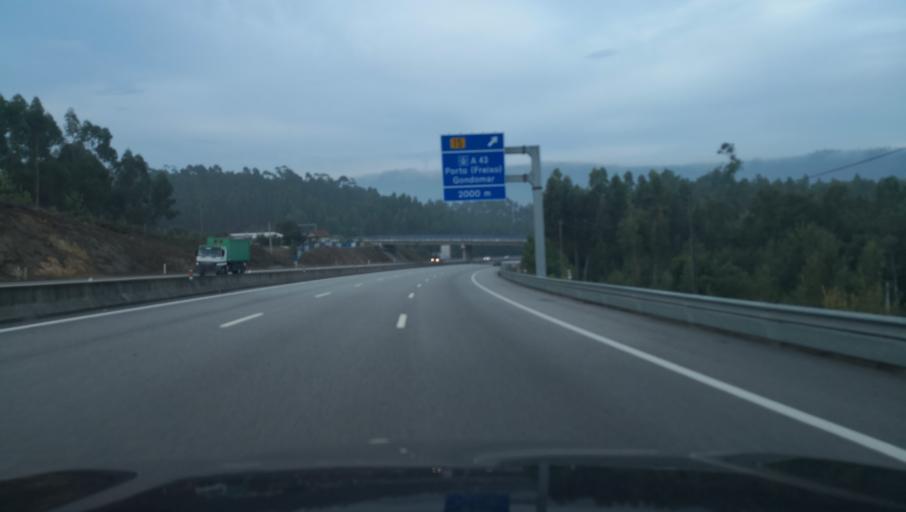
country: PT
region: Porto
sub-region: Paredes
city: Recarei
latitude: 41.1105
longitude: -8.4325
